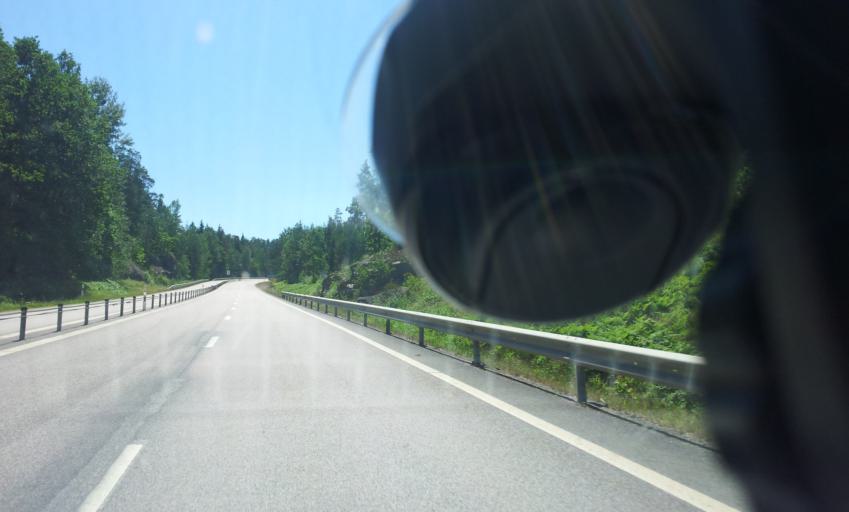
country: SE
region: Kalmar
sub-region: Vasterviks Kommun
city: Forserum
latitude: 58.0478
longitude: 16.5237
